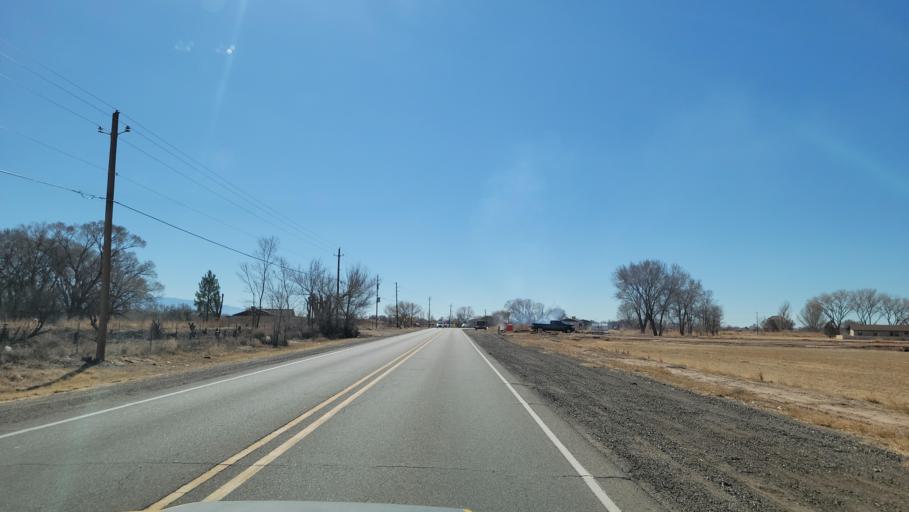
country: US
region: New Mexico
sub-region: Bernalillo County
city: South Valley
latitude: 34.9398
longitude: -106.6919
